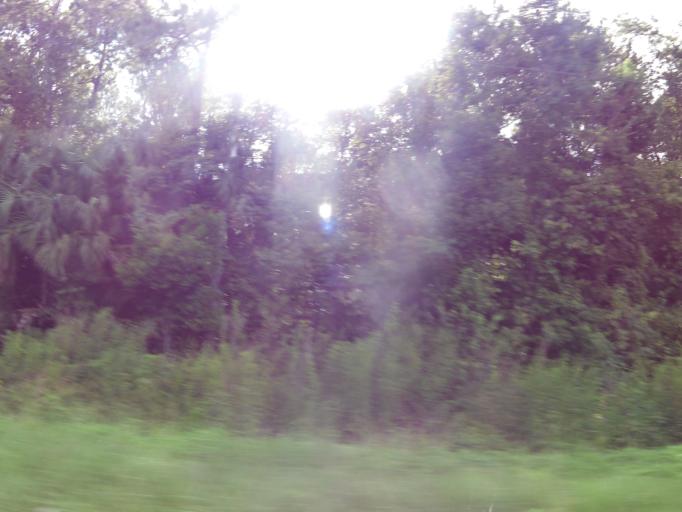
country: US
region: Florida
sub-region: Clay County
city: Green Cove Springs
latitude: 29.9747
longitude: -81.6931
